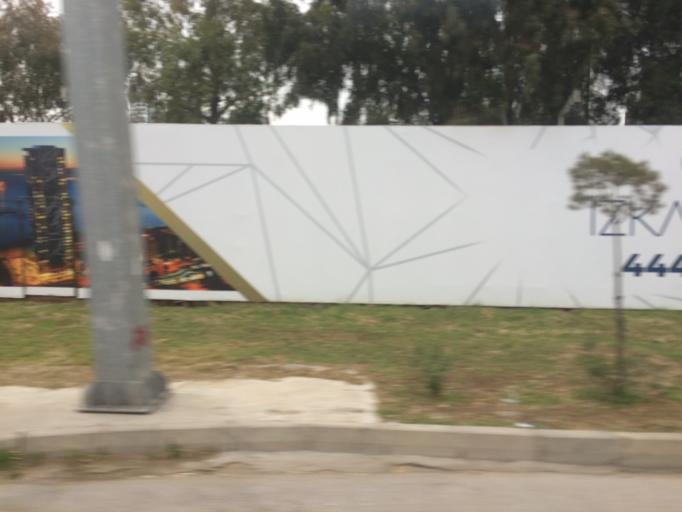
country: TR
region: Izmir
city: Izmir
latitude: 38.4476
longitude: 27.1716
